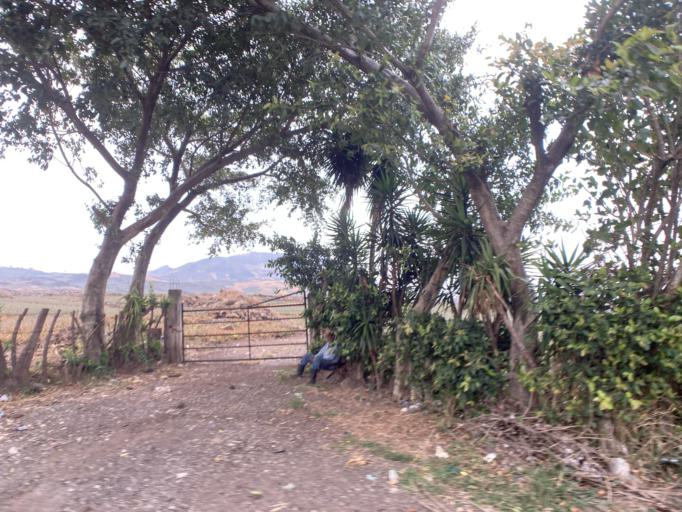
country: GT
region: Guatemala
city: Fraijanes
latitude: 14.3691
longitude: -90.4921
